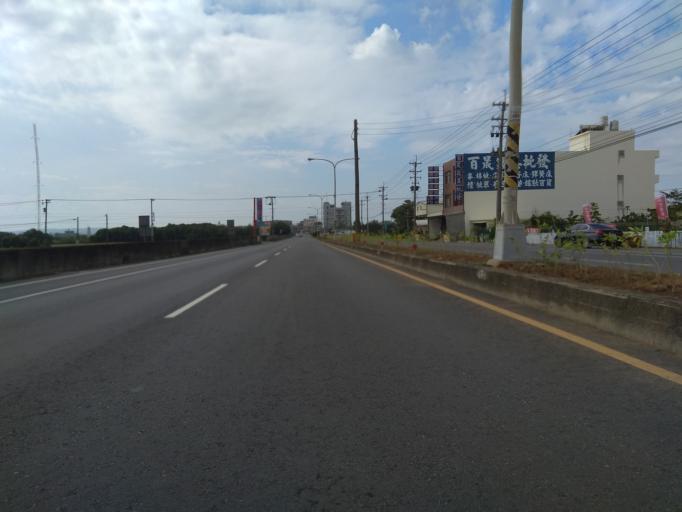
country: TW
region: Taiwan
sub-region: Hsinchu
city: Zhubei
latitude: 24.9295
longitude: 120.9940
